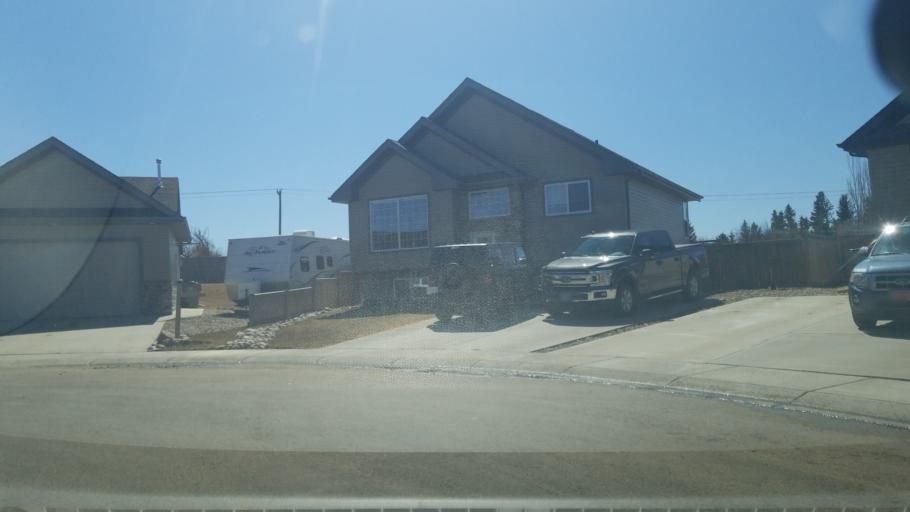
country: CA
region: Saskatchewan
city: Lloydminster
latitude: 53.2496
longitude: -110.0186
